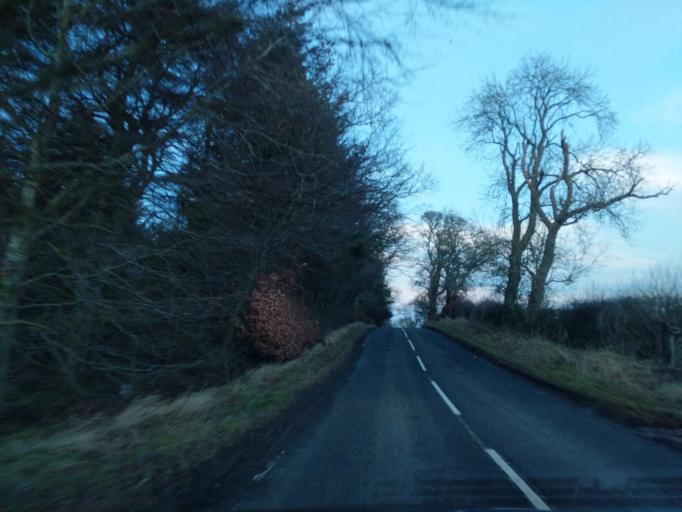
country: GB
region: Scotland
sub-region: Midlothian
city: Bonnyrigg
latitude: 55.8113
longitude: -3.1067
